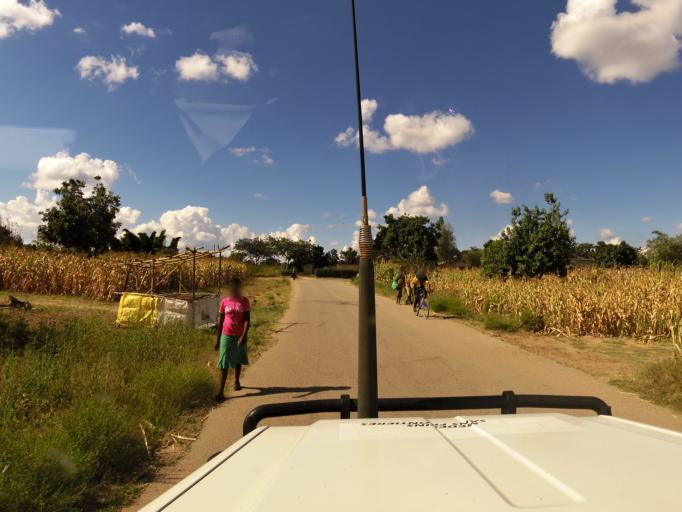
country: ZW
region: Harare
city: Epworth
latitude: -17.8708
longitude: 31.1352
